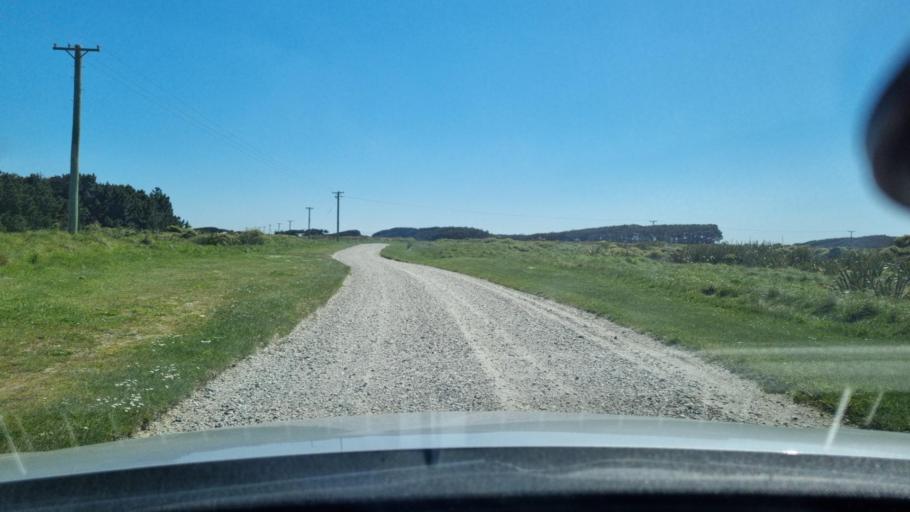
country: NZ
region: Southland
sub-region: Invercargill City
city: Invercargill
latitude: -46.4362
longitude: 168.2380
